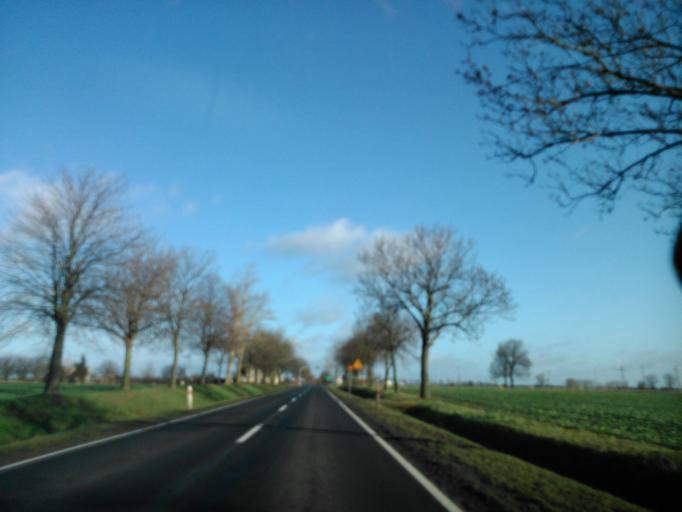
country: PL
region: Kujawsko-Pomorskie
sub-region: Powiat inowroclawski
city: Wierzchoslawice
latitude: 52.8662
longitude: 18.3632
